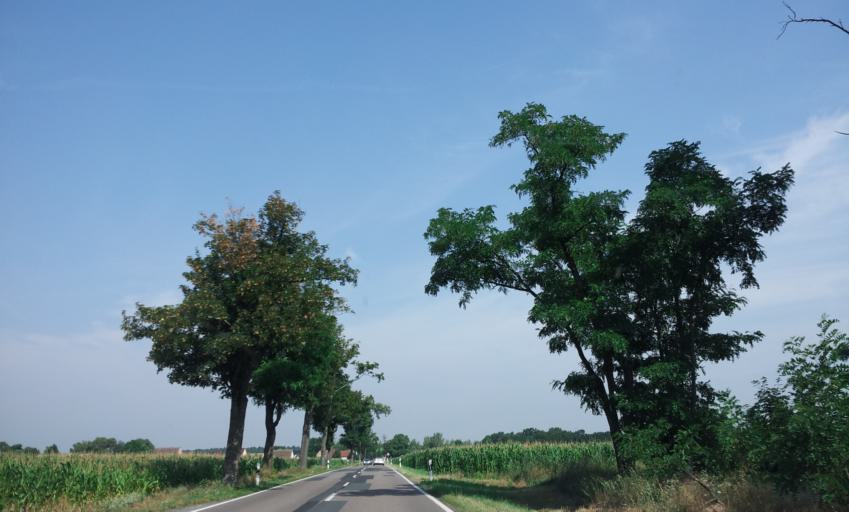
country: DE
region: Brandenburg
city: Linthe
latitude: 52.1269
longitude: 12.8013
